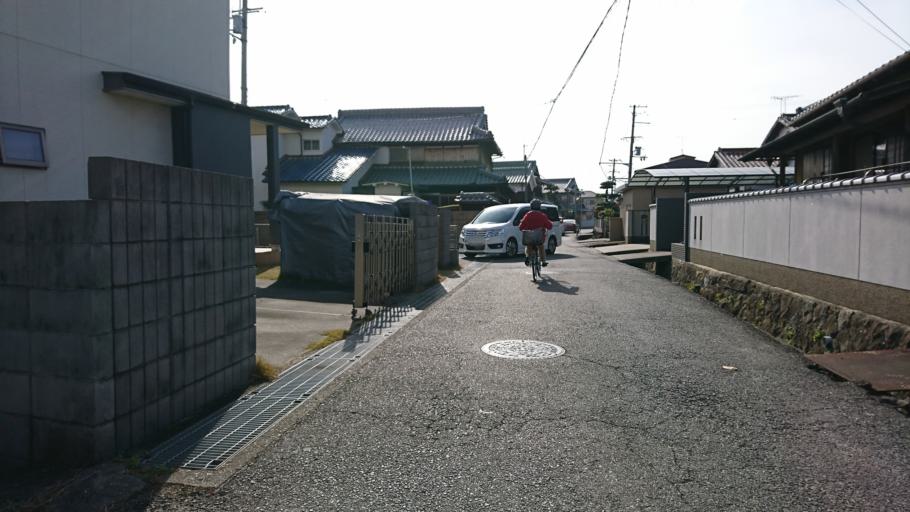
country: JP
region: Hyogo
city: Kakogawacho-honmachi
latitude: 34.7478
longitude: 134.8466
